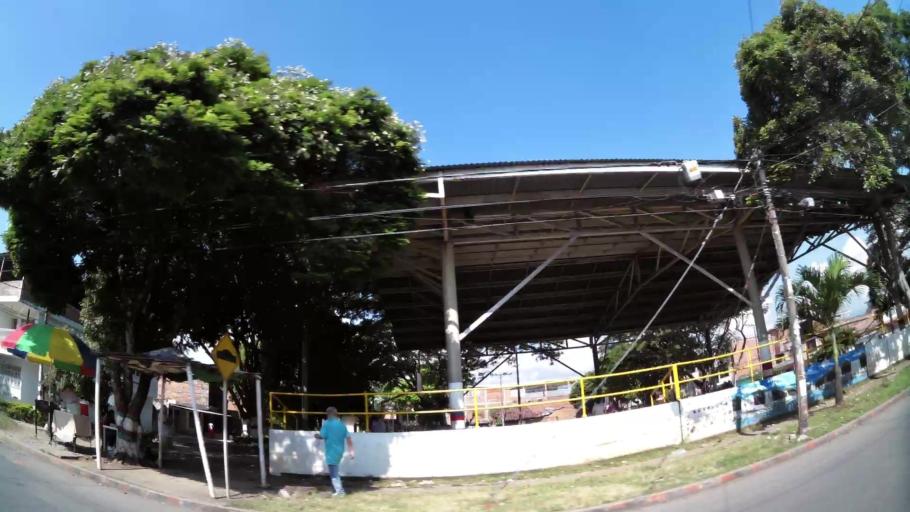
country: CO
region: Valle del Cauca
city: Cali
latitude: 3.4065
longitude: -76.5234
